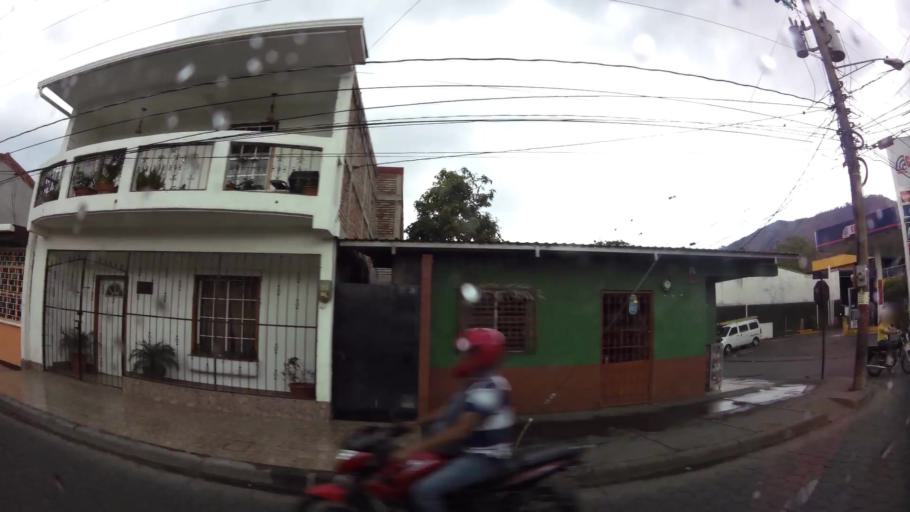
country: NI
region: Jinotega
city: Jinotega
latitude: 13.0888
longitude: -86.0002
